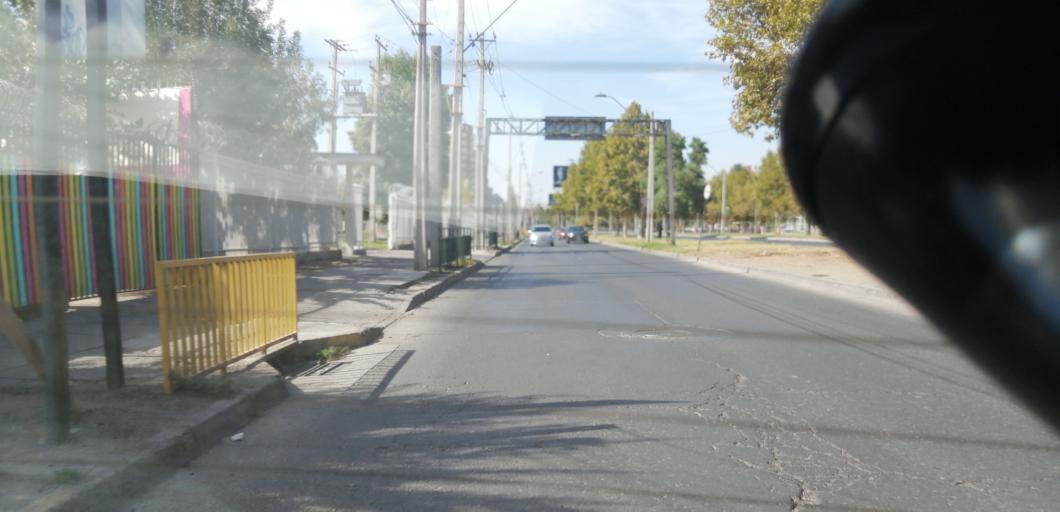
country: CL
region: Santiago Metropolitan
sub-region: Provincia de Santiago
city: Lo Prado
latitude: -33.4663
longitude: -70.7289
